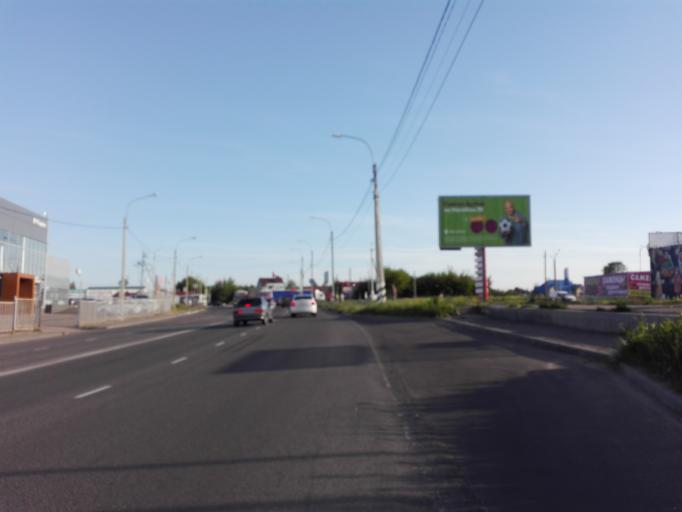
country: RU
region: Orjol
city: Orel
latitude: 52.9484
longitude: 36.0239
